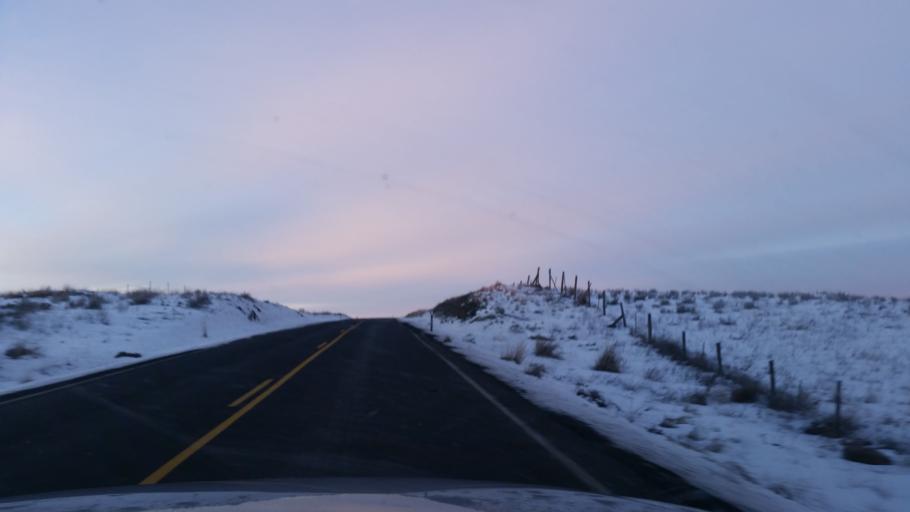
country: US
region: Washington
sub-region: Spokane County
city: Medical Lake
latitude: 47.2203
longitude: -117.9011
